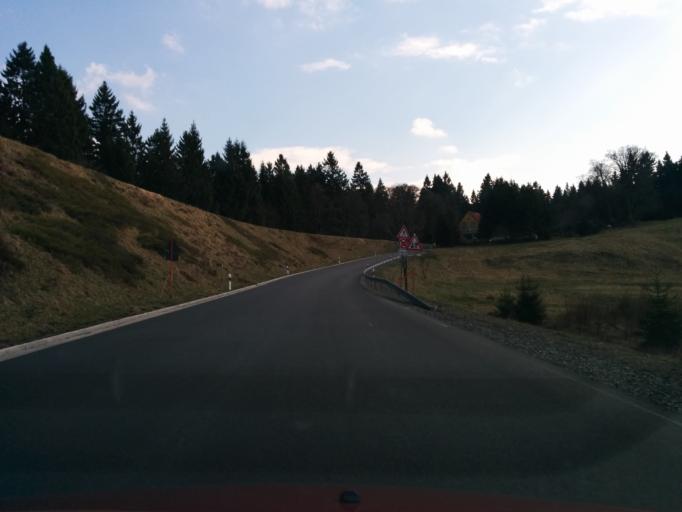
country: DE
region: Lower Saxony
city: Altenau
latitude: 51.7791
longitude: 10.4212
